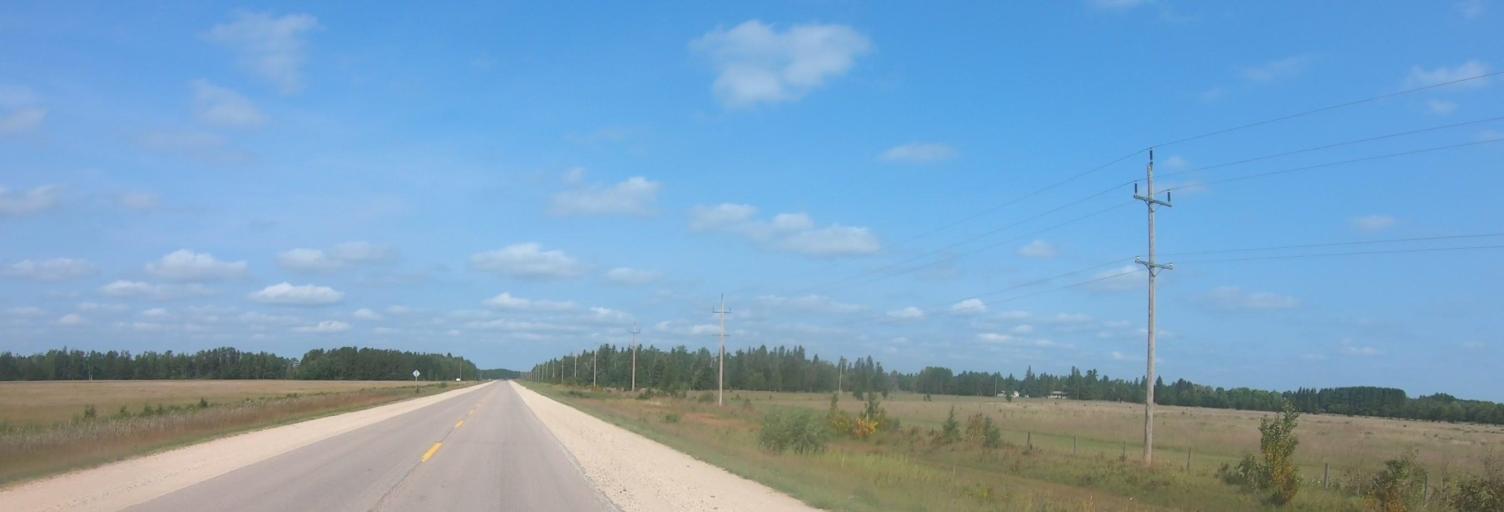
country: CA
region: Manitoba
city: La Broquerie
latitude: 49.1796
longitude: -96.2330
